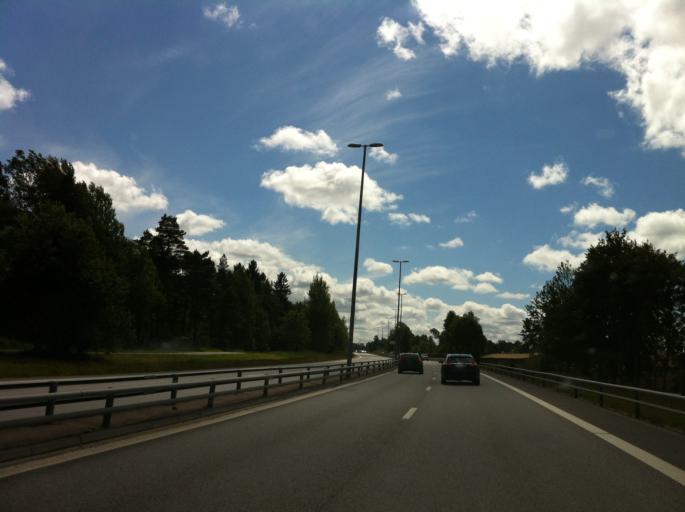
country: SE
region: Vaestra Goetaland
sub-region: Trollhattan
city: Trollhattan
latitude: 58.2805
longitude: 12.3053
